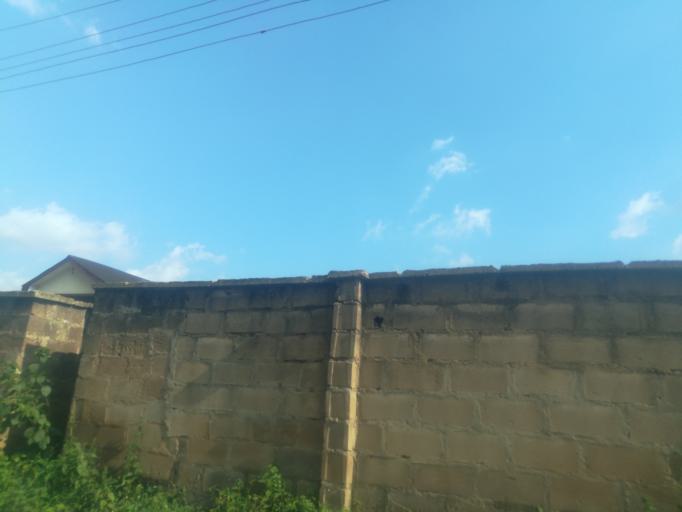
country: NG
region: Oyo
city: Ibadan
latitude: 7.4185
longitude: 3.8354
